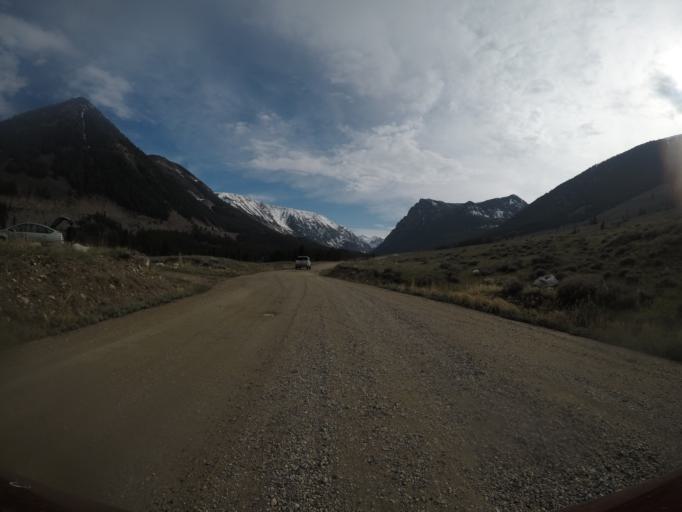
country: US
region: Montana
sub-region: Carbon County
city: Red Lodge
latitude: 45.0567
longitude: -109.4161
